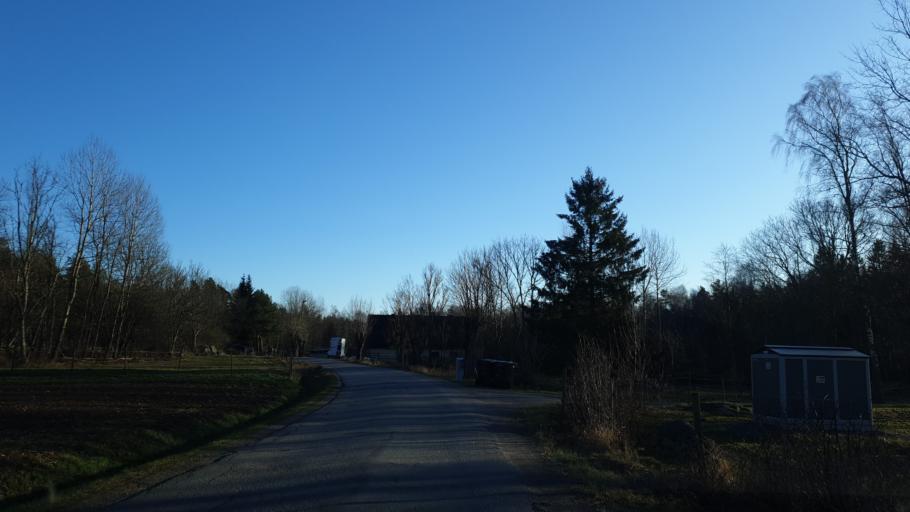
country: SE
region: Blekinge
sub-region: Ronneby Kommun
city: Brakne-Hoby
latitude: 56.2286
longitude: 15.1698
